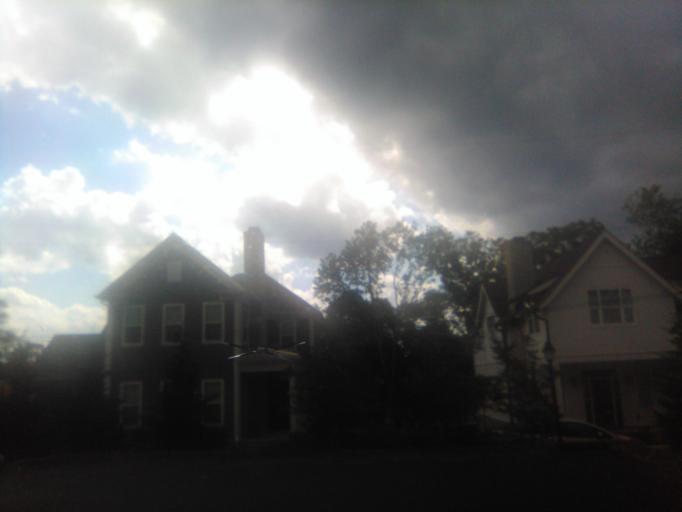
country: US
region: Tennessee
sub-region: Davidson County
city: Belle Meade
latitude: 36.1027
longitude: -86.8296
